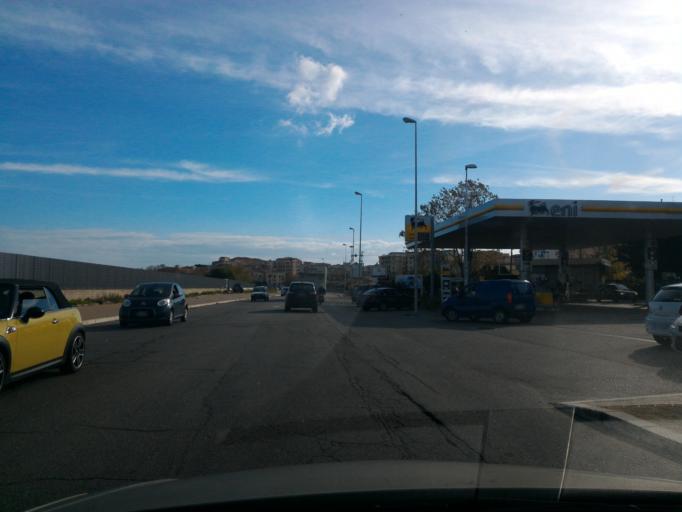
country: IT
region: Calabria
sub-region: Provincia di Crotone
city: Crotone
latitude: 39.0853
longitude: 17.1222
